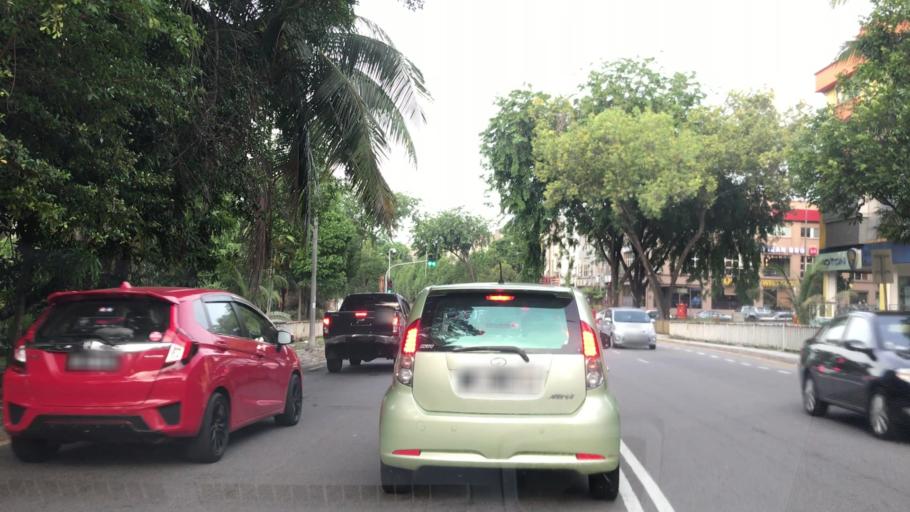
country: MY
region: Kuala Lumpur
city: Kuala Lumpur
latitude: 3.0717
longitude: 101.6907
